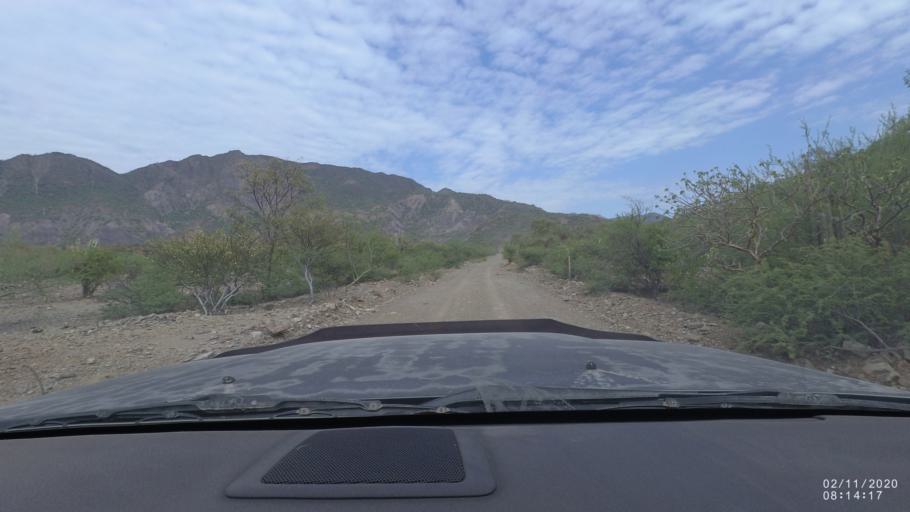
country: BO
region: Chuquisaca
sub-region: Provincia Zudanez
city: Mojocoya
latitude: -18.6254
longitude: -64.5369
